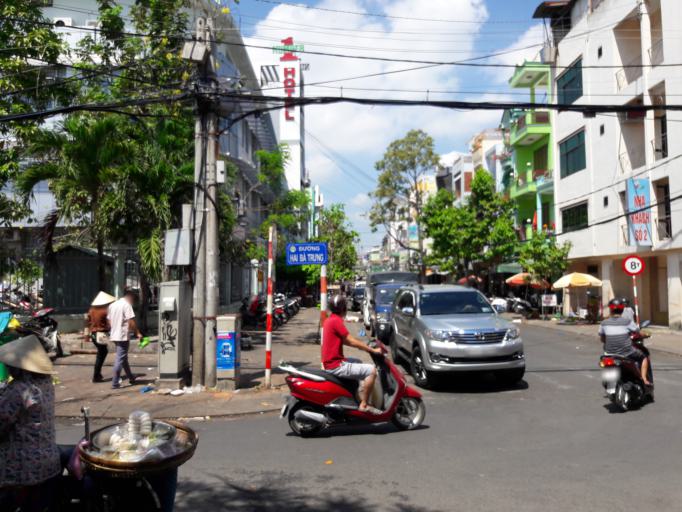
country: VN
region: Can Tho
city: Can Tho
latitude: 10.0299
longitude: 105.7877
